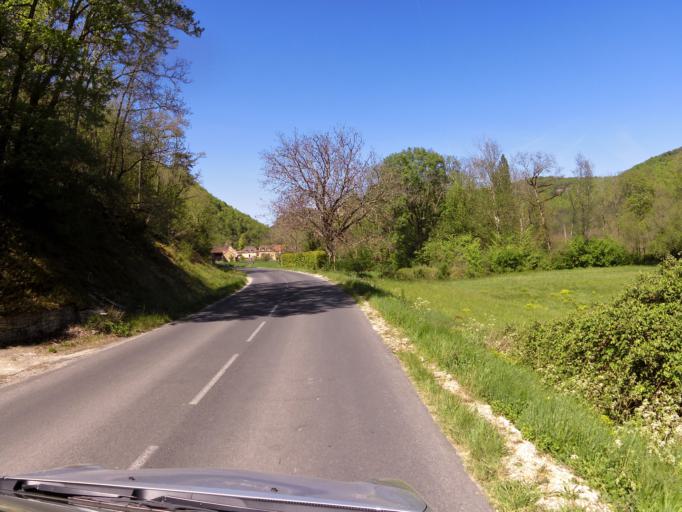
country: FR
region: Aquitaine
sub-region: Departement de la Dordogne
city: Cenac-et-Saint-Julien
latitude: 44.7934
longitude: 1.1617
